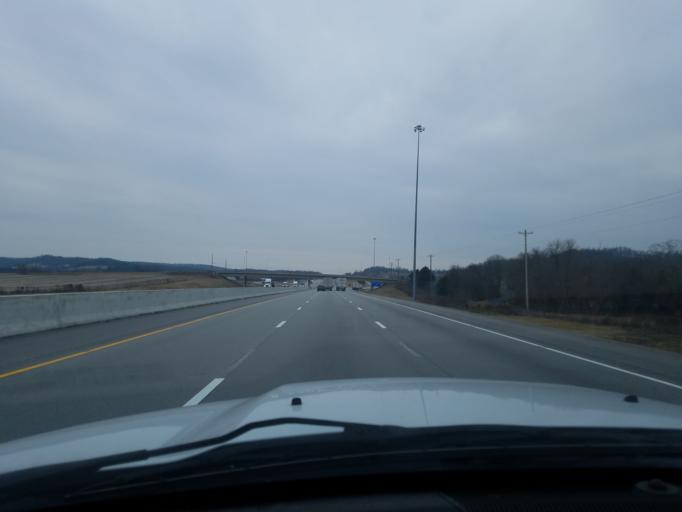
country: US
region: Kentucky
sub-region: Hart County
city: Munfordville
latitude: 37.2464
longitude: -85.9264
